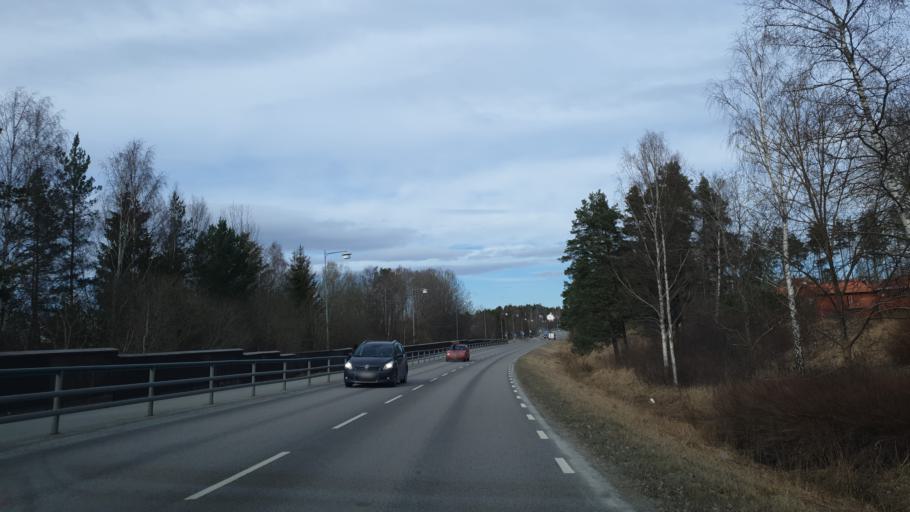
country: SE
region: Stockholm
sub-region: Vallentuna Kommun
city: Vallentuna
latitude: 59.5143
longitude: 18.0675
